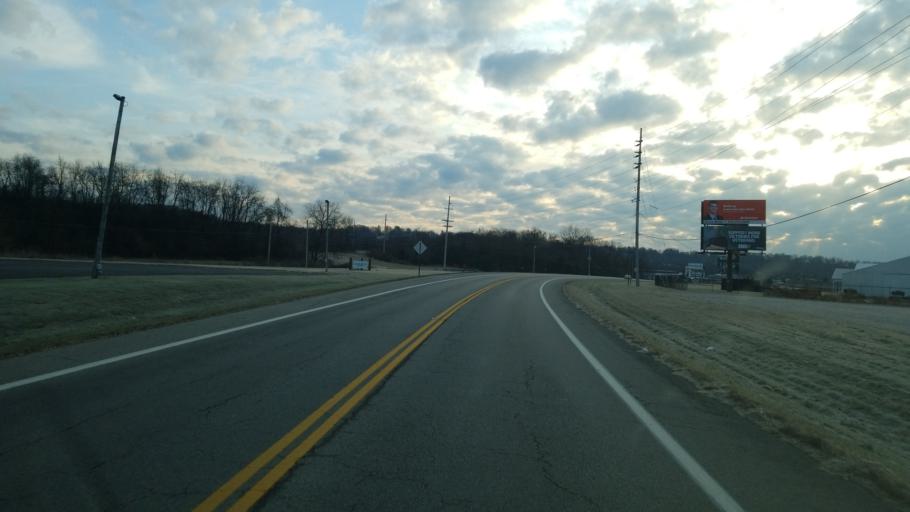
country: US
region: Ohio
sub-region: Ross County
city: North Fork Village
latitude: 39.3493
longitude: -83.0454
